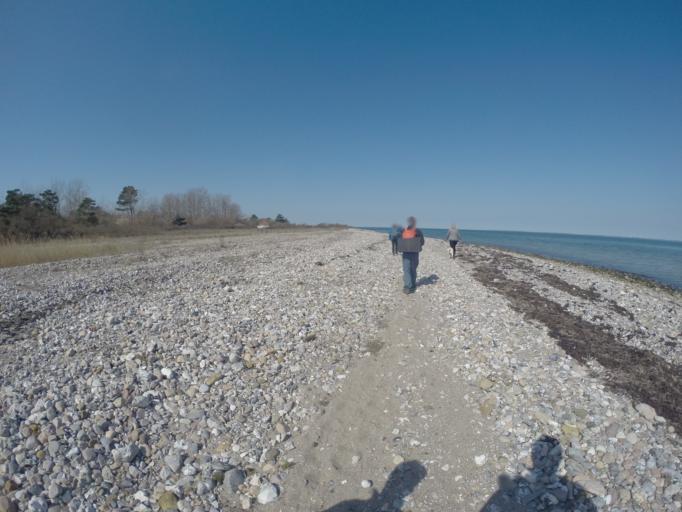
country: DK
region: Zealand
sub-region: Kalundborg Kommune
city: Gorlev
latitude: 55.5359
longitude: 11.1282
